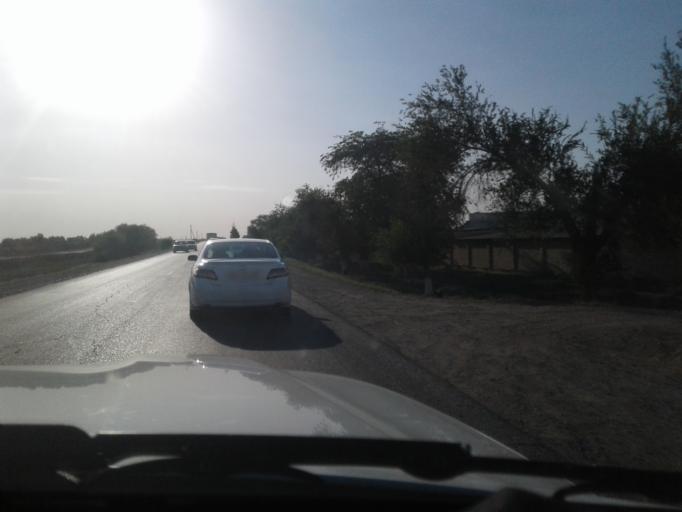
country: TM
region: Mary
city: Yoloeten
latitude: 37.2888
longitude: 62.3477
